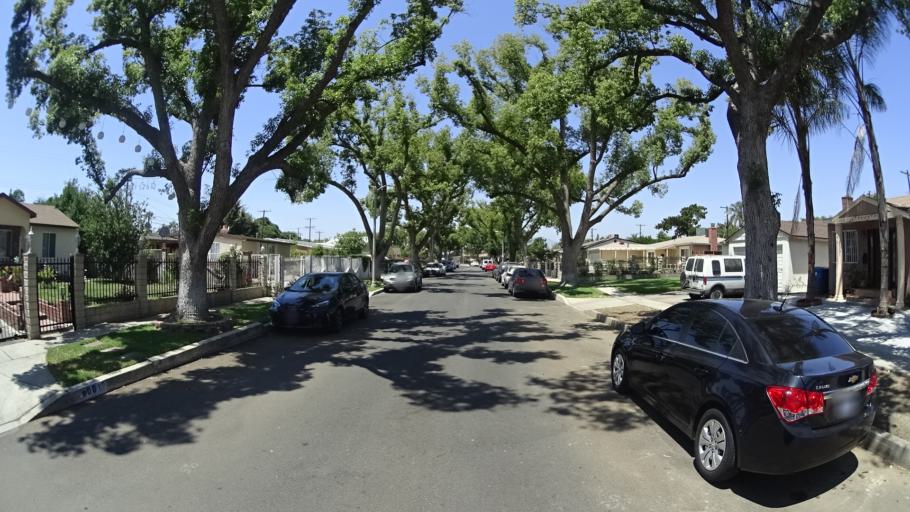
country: US
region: California
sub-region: Los Angeles County
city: Van Nuys
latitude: 34.2160
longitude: -118.4340
